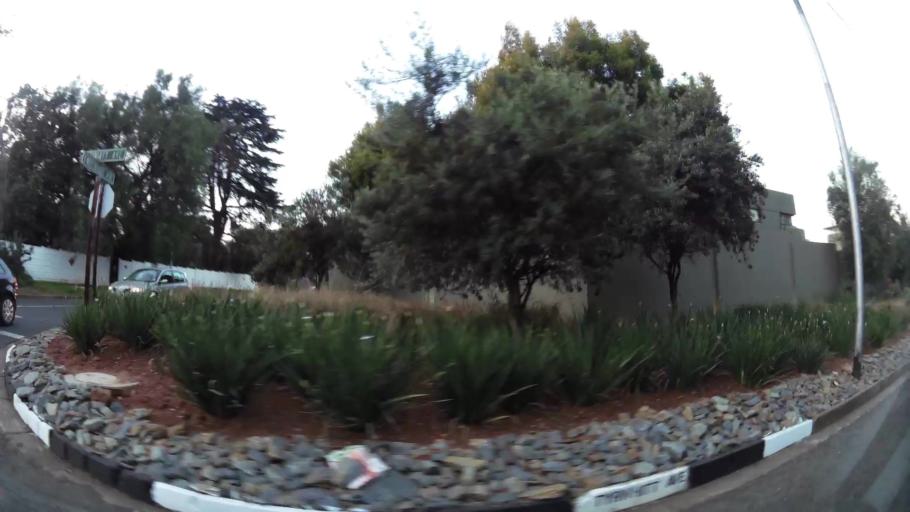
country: ZA
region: Gauteng
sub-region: City of Johannesburg Metropolitan Municipality
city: Johannesburg
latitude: -26.1438
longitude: 28.0556
